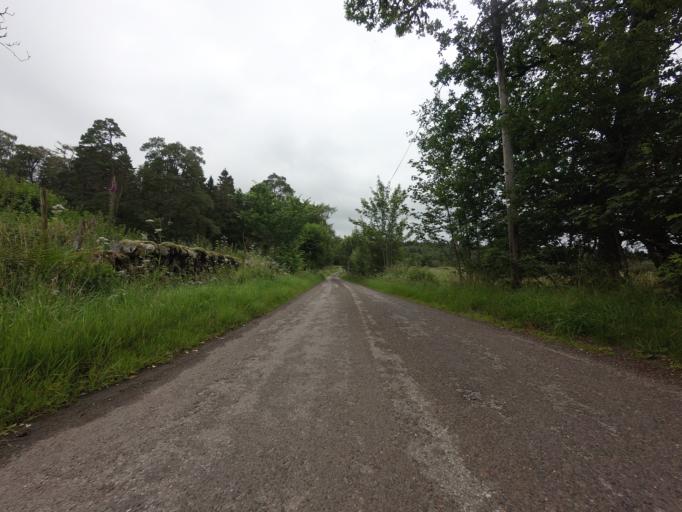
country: GB
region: Scotland
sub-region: Highland
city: Evanton
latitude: 57.9815
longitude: -4.4169
